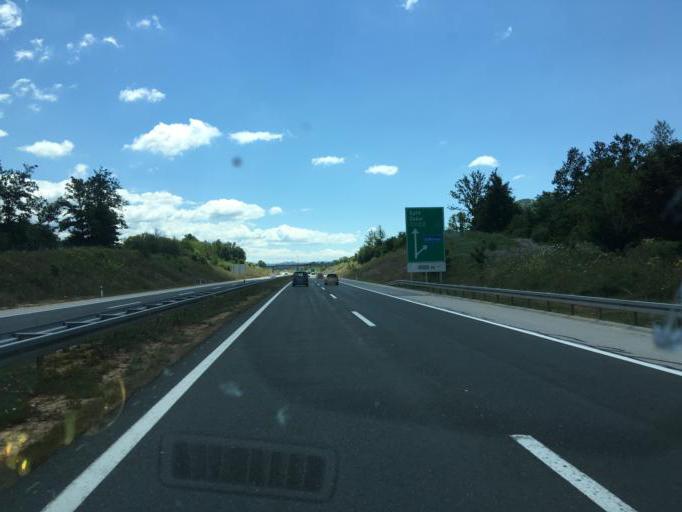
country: HR
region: Zadarska
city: Starigrad
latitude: 44.4490
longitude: 15.6143
